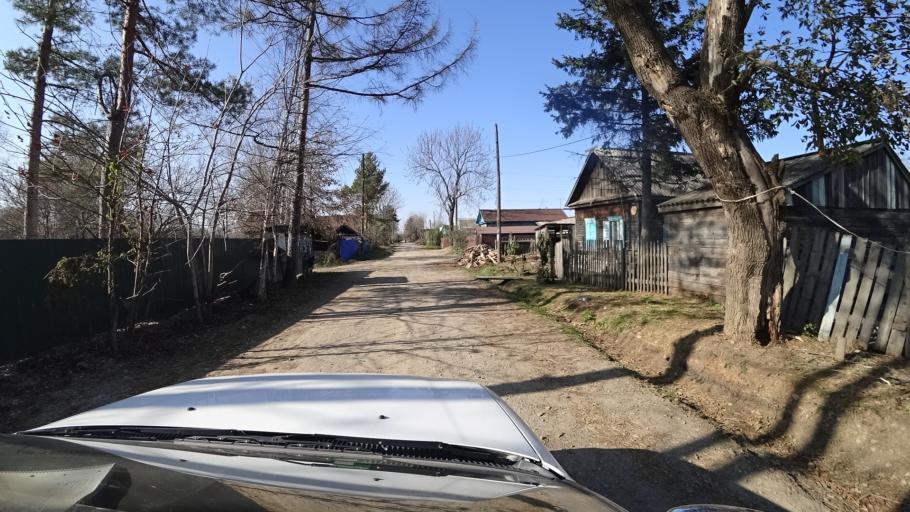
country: RU
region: Primorskiy
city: Dal'nerechensk
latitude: 45.9277
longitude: 133.7168
